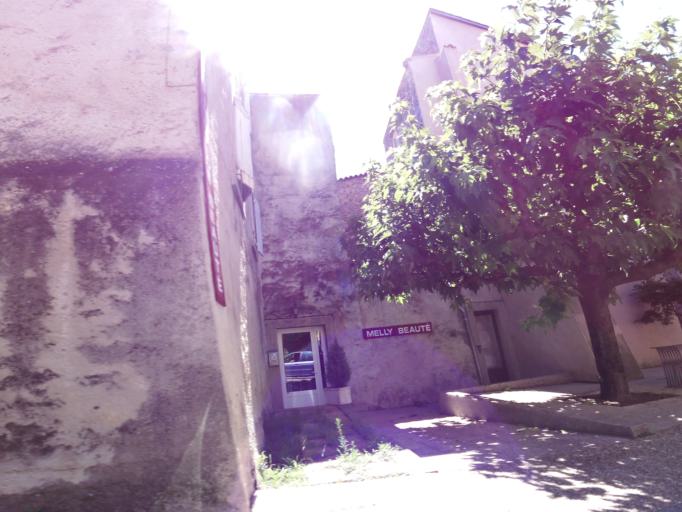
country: FR
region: Languedoc-Roussillon
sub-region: Departement du Gard
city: Saint-Jean-du-Gard
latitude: 44.1057
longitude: 3.8852
